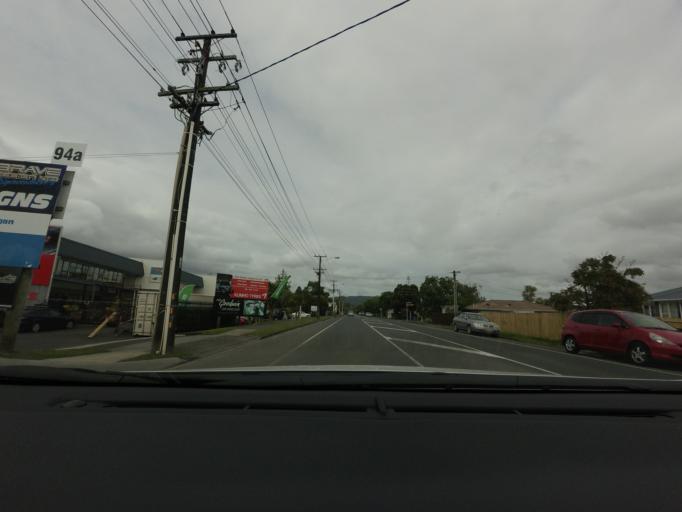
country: NZ
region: Auckland
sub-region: Auckland
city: Waitakere
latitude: -36.8899
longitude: 174.6253
